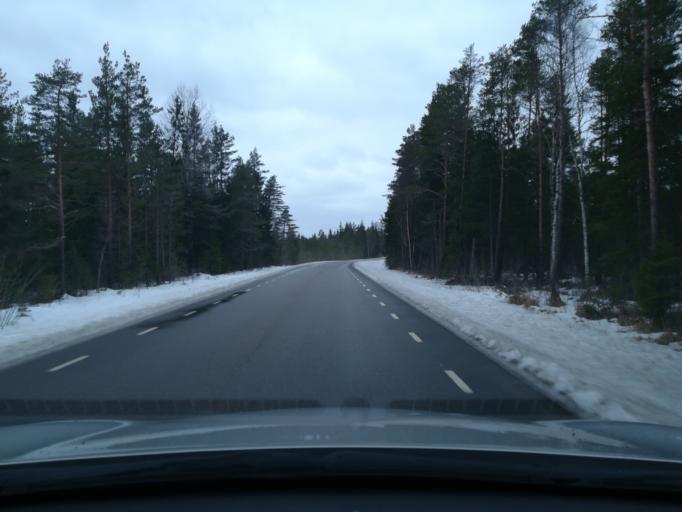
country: EE
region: Harju
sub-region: Nissi vald
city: Riisipere
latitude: 59.1404
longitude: 24.2973
